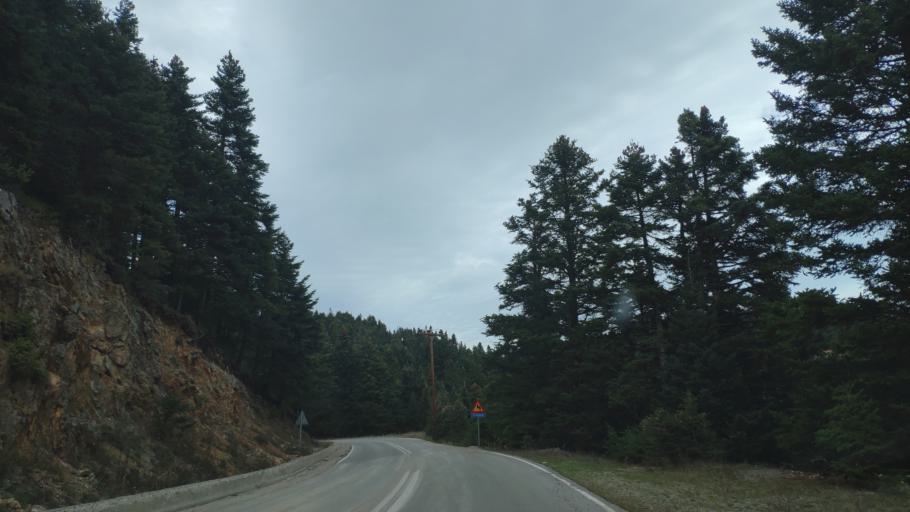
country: GR
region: Central Greece
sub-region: Nomos Fokidos
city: Amfissa
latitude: 38.6995
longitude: 22.3115
